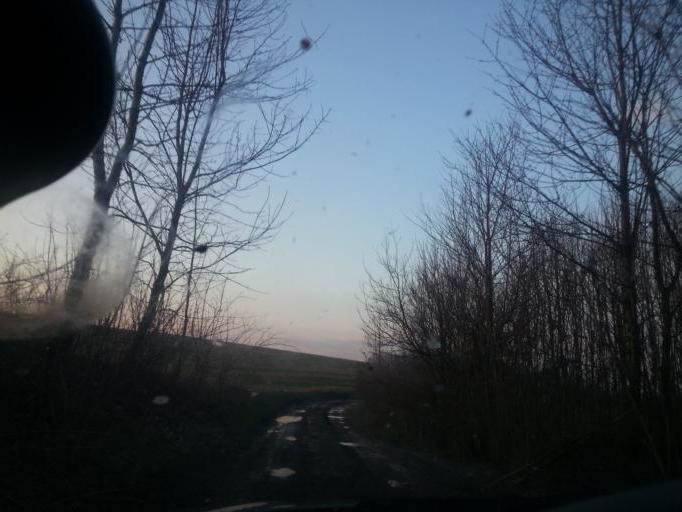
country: PL
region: Lower Silesian Voivodeship
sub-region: Powiat jeleniogorski
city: Stara Kamienica
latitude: 50.9570
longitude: 15.6239
